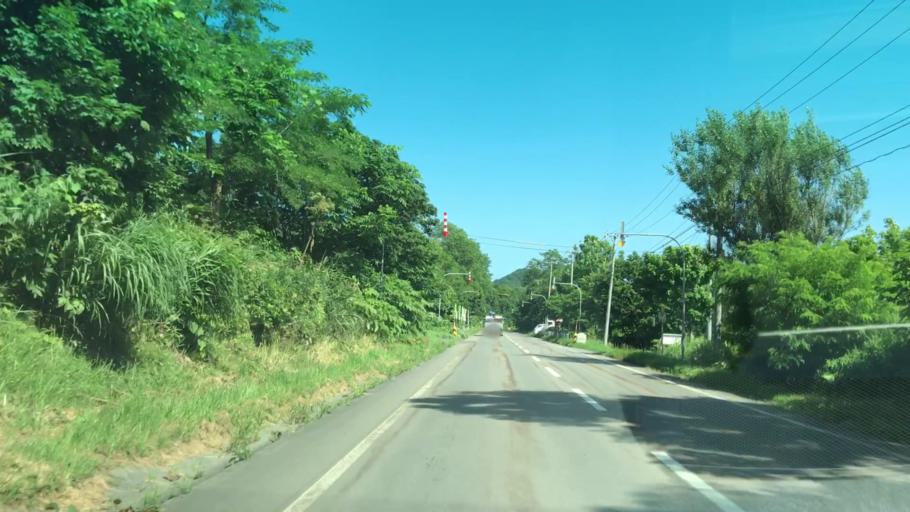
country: JP
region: Hokkaido
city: Iwanai
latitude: 43.0782
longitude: 140.4832
